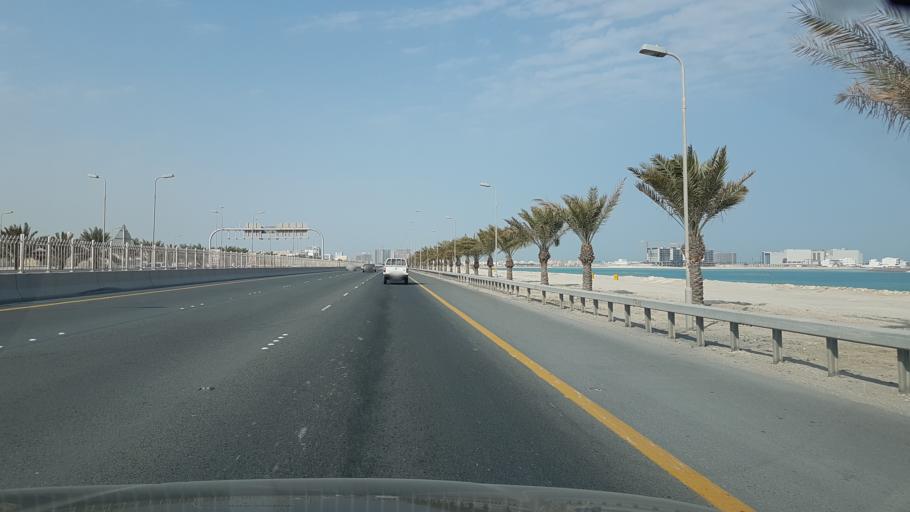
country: BH
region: Muharraq
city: Al Hadd
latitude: 26.2575
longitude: 50.6605
